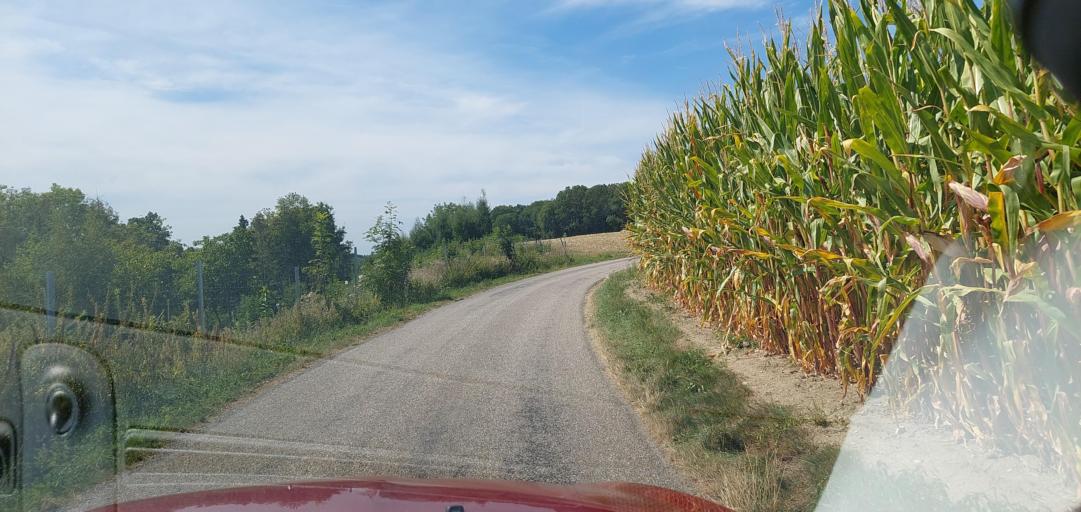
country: AT
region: Upper Austria
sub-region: Wels-Land
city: Offenhausen
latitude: 48.1423
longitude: 13.8370
